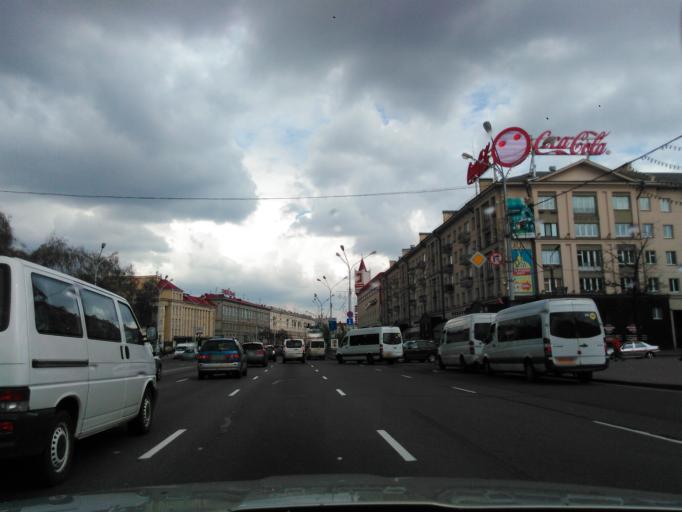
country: BY
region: Minsk
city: Minsk
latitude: 53.9152
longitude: 27.5833
